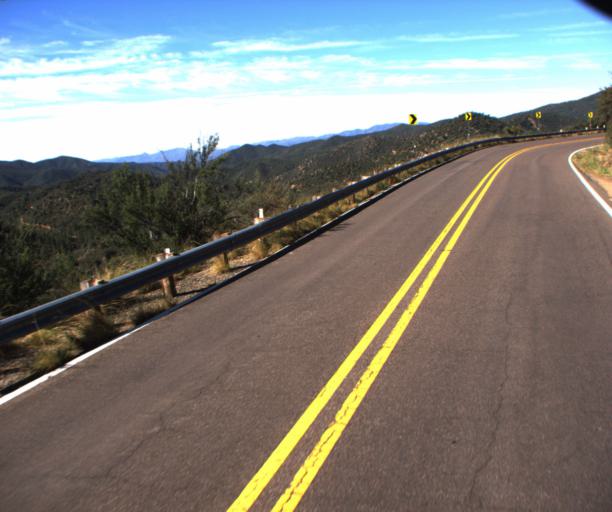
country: US
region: Arizona
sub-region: Yavapai County
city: Prescott
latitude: 34.4577
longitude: -112.5203
